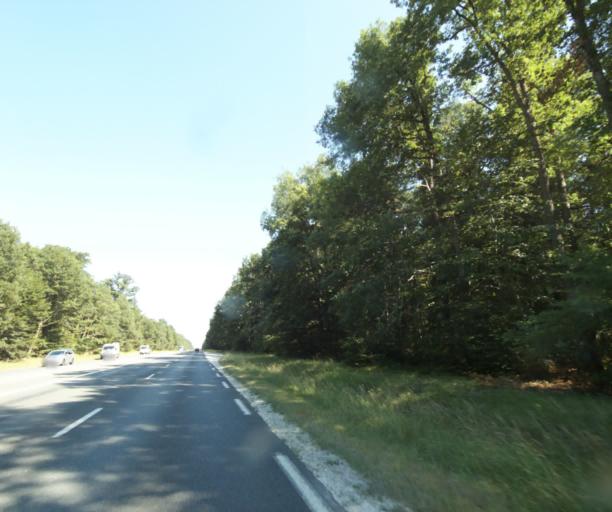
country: FR
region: Ile-de-France
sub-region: Departement de Seine-et-Marne
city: Thomery
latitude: 48.3885
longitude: 2.7587
